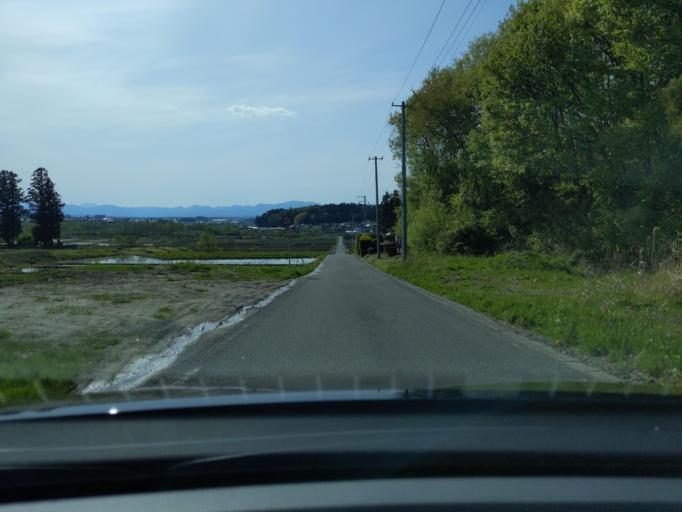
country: JP
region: Fukushima
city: Sukagawa
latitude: 37.2988
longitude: 140.4116
